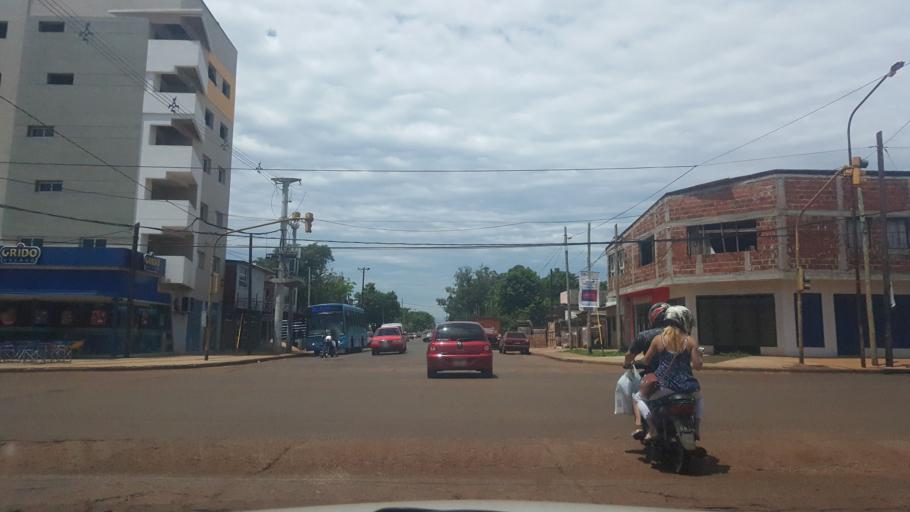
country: AR
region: Misiones
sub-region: Departamento de Capital
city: Posadas
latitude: -27.3789
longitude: -55.9184
